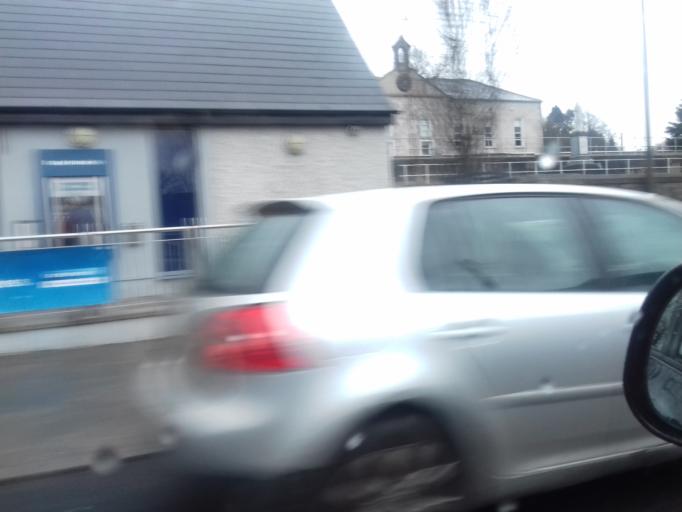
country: IE
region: Leinster
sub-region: Kilkenny
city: Graiguenamanagh
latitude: 52.5424
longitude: -6.9564
